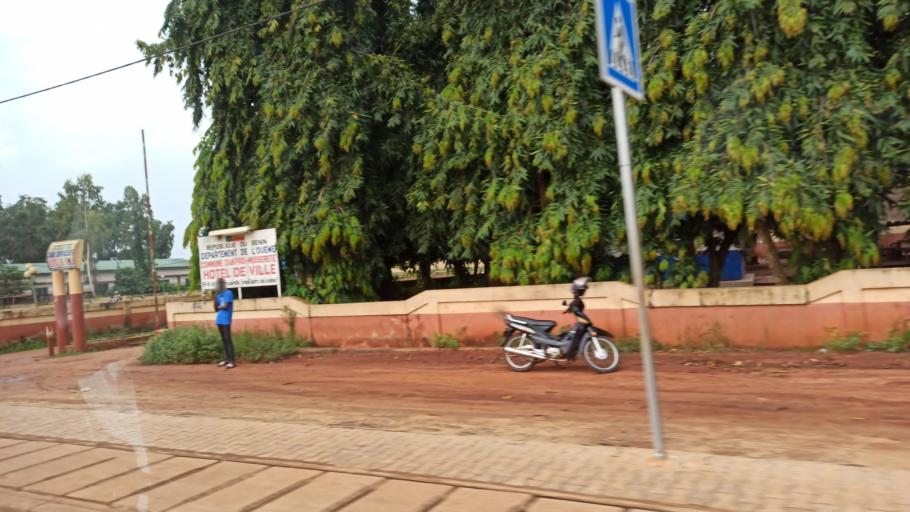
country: BJ
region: Queme
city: Porto-Novo
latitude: 6.5573
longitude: 2.5886
